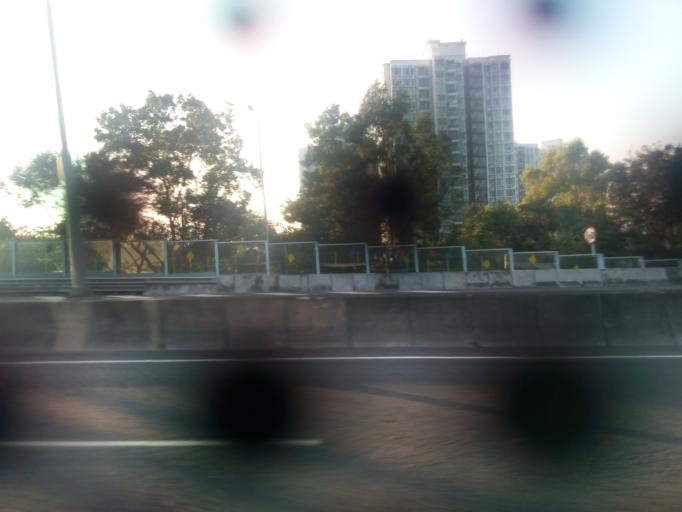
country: HK
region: Yuen Long
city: Yuen Long Kau Hui
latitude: 22.4334
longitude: 114.0031
